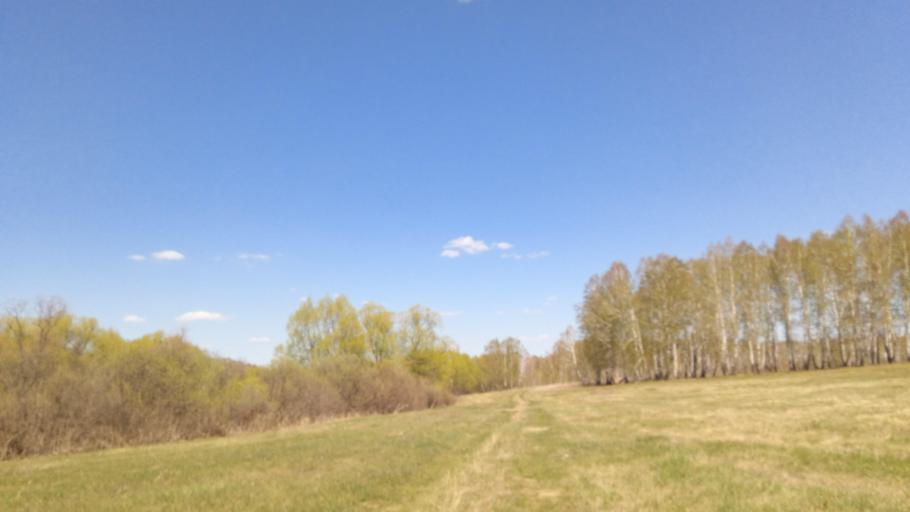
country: RU
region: Chelyabinsk
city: Timiryazevskiy
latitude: 54.9987
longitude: 60.8512
